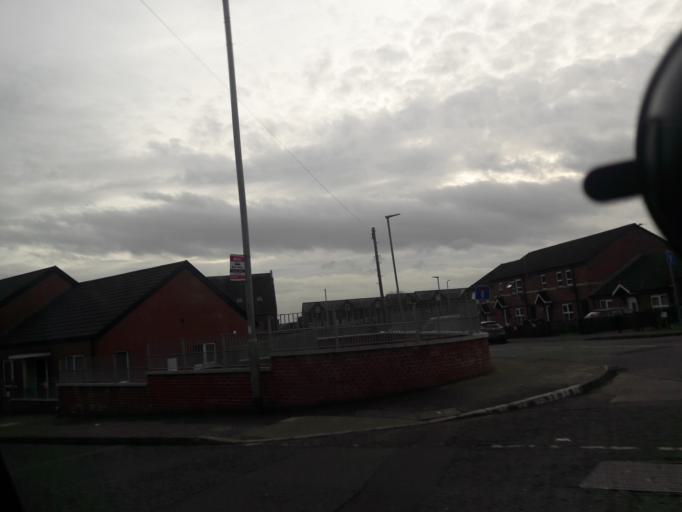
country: GB
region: Northern Ireland
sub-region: City of Belfast
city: Belfast
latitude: 54.6108
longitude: -5.9479
